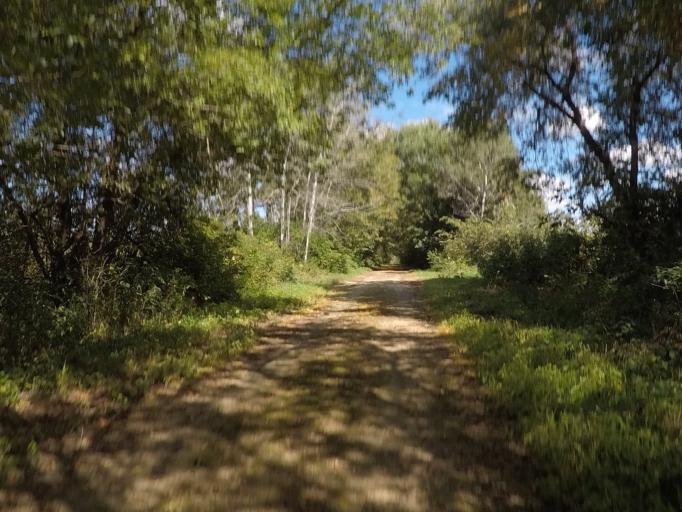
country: US
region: Wisconsin
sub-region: Richland County
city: Richland Center
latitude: 43.2477
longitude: -90.3048
